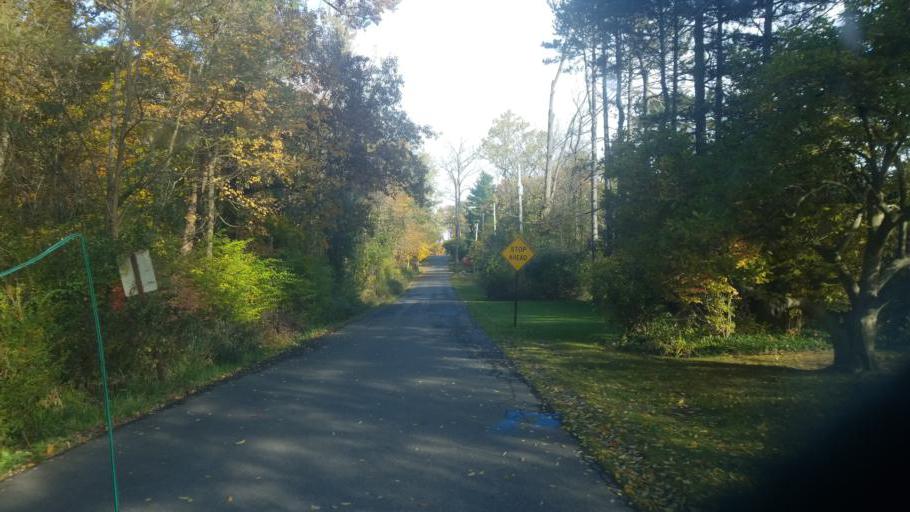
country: US
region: Ohio
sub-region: Richland County
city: Mansfield
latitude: 40.7400
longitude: -82.5422
